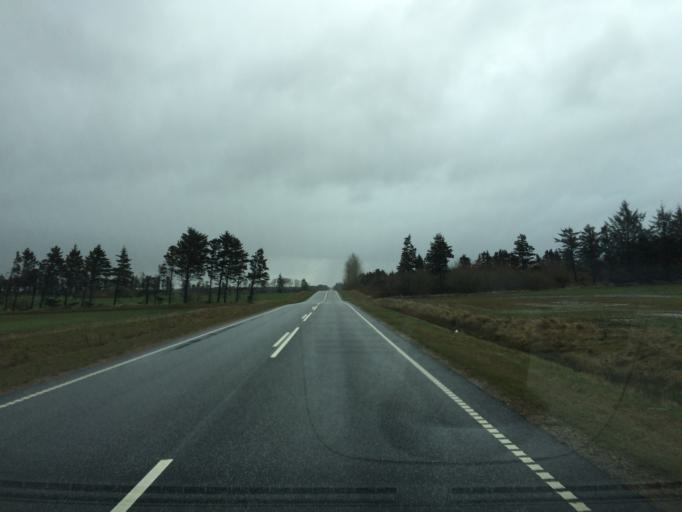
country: DK
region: Central Jutland
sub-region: Ringkobing-Skjern Kommune
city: Videbaek
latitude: 56.1879
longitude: 8.6150
